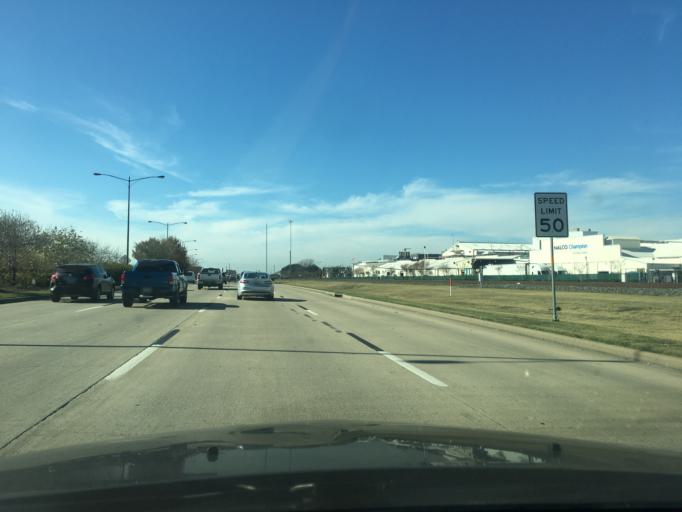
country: US
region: Texas
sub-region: Fort Bend County
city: Sugar Land
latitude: 29.6190
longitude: -95.6384
